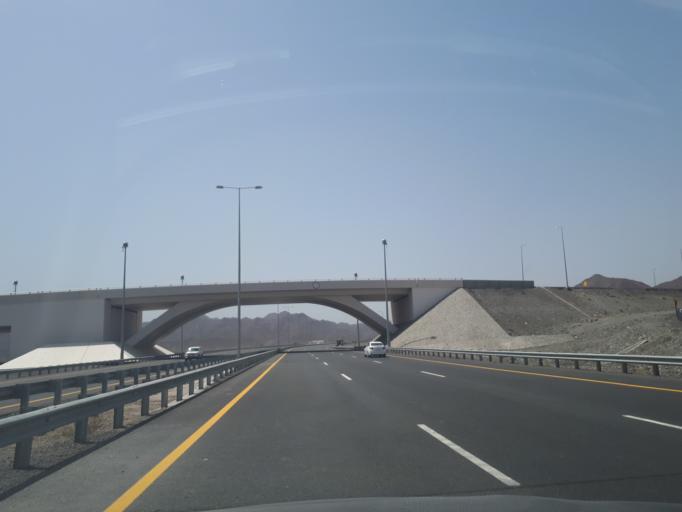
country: OM
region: Muhafazat ad Dakhiliyah
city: Bidbid
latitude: 23.3300
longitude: 58.1147
